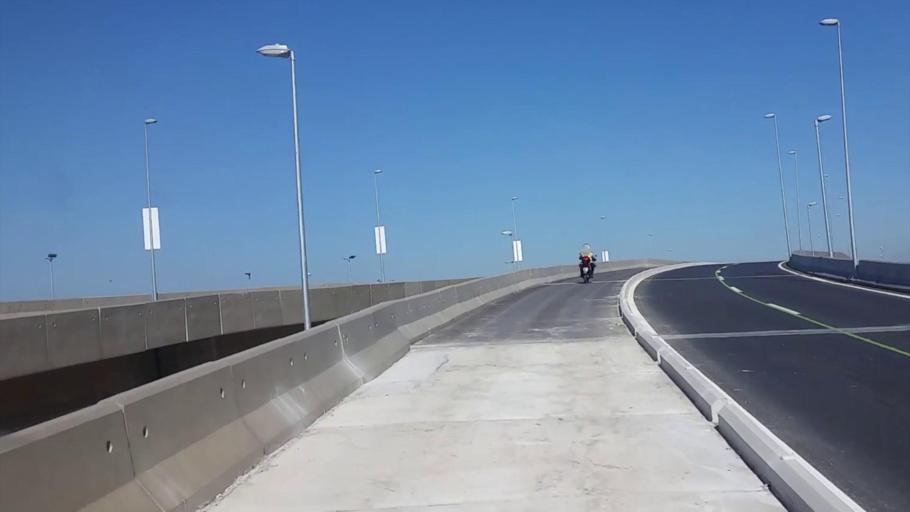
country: BR
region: Rio de Janeiro
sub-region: Nilopolis
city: Nilopolis
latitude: -22.9654
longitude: -43.3959
